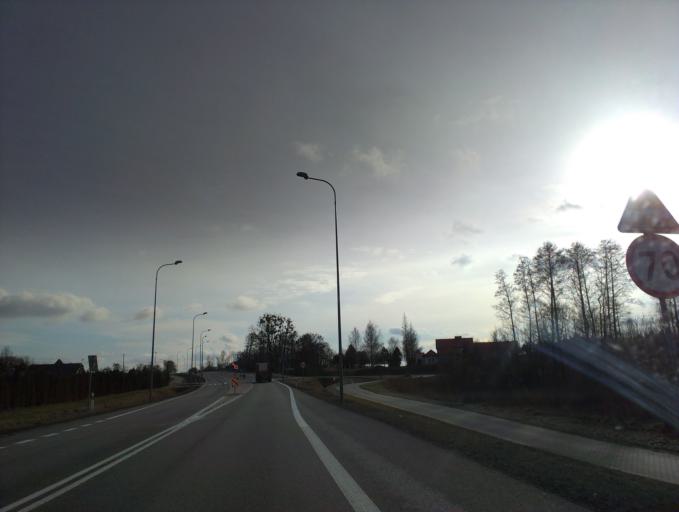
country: PL
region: Kujawsko-Pomorskie
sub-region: Powiat lipnowski
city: Lipno
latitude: 52.8614
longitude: 19.1560
